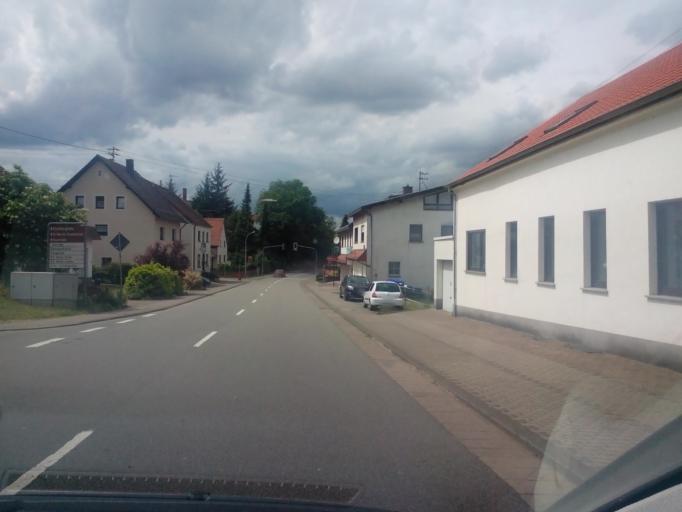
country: DE
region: Saarland
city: Eppelborn
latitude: 49.4096
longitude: 6.9494
